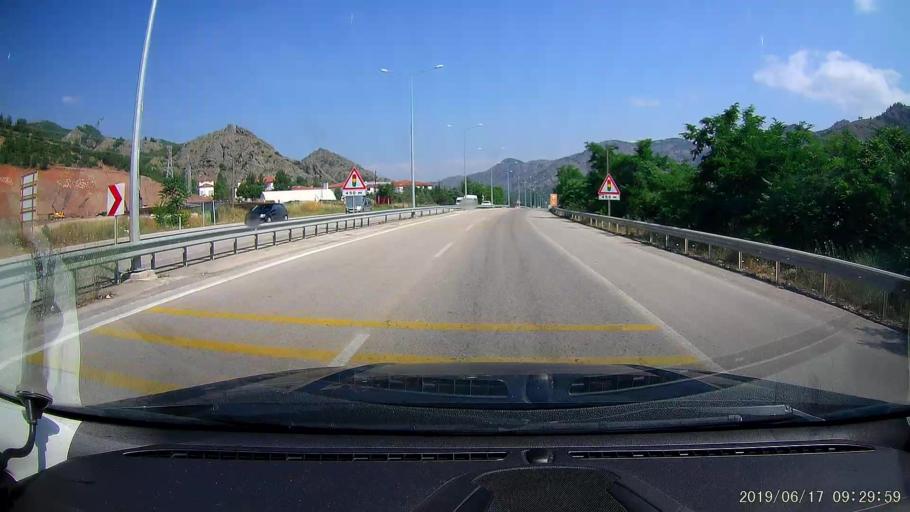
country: TR
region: Amasya
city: Amasya
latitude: 40.7011
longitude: 35.8062
